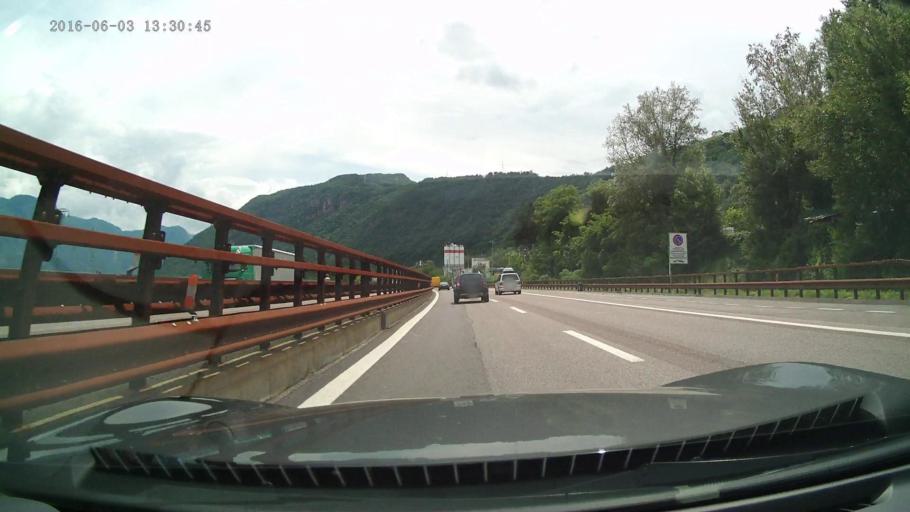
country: IT
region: Trentino-Alto Adige
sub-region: Bolzano
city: Cornaiano
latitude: 46.4617
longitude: 11.3042
